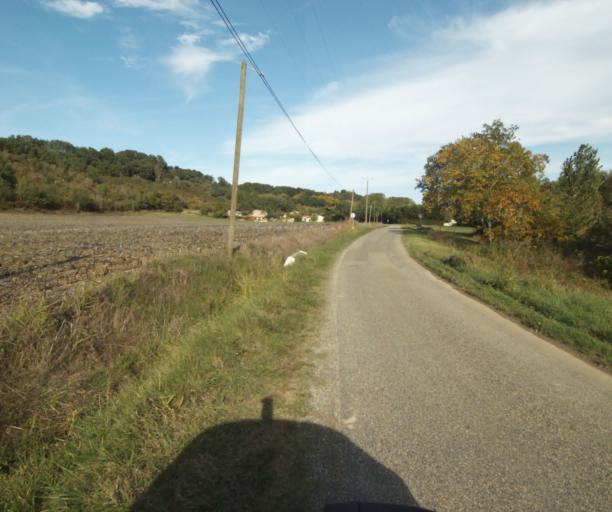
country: FR
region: Midi-Pyrenees
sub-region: Departement du Tarn-et-Garonne
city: Saint-Porquier
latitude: 43.9405
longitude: 1.1547
